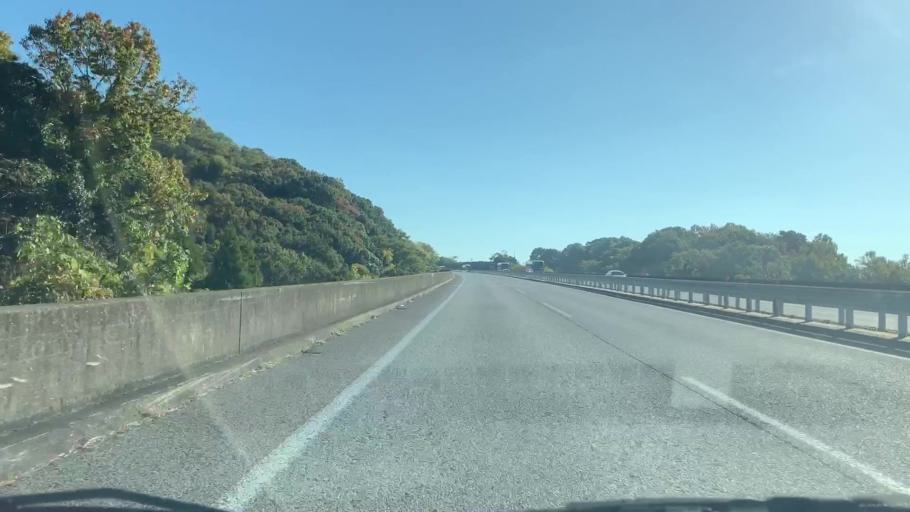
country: JP
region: Saga Prefecture
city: Saga-shi
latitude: 33.2871
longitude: 130.1492
